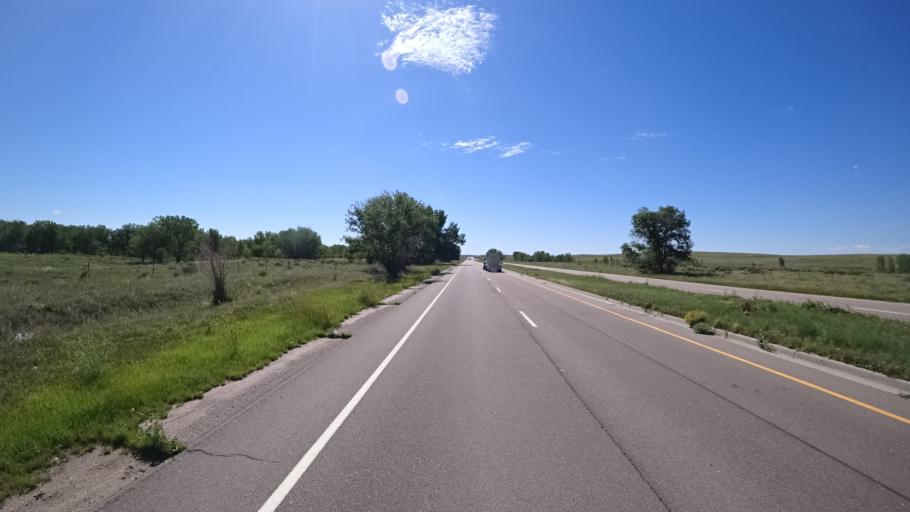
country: US
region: Colorado
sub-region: El Paso County
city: Security-Widefield
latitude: 38.7549
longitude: -104.6575
